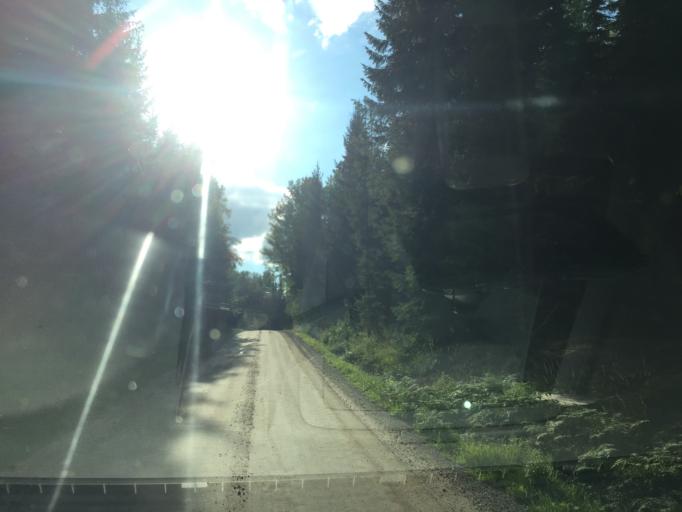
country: SE
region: Soedermanland
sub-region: Vingakers Kommun
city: Vingaker
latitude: 59.0057
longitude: 15.7591
